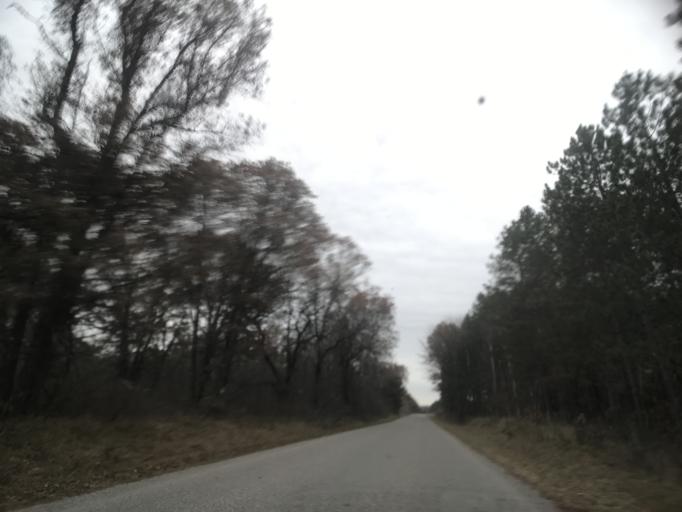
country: US
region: Wisconsin
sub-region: Oconto County
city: Gillett
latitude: 45.3423
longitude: -88.2861
